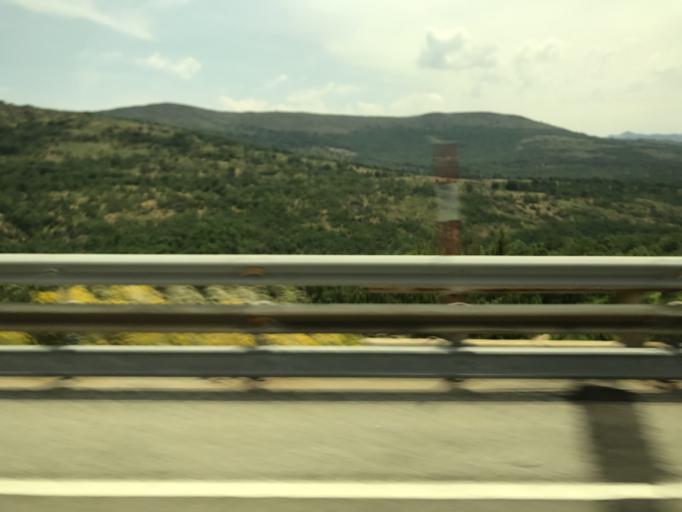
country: ES
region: Madrid
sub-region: Provincia de Madrid
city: Robregordo
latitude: 41.0975
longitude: -3.5924
